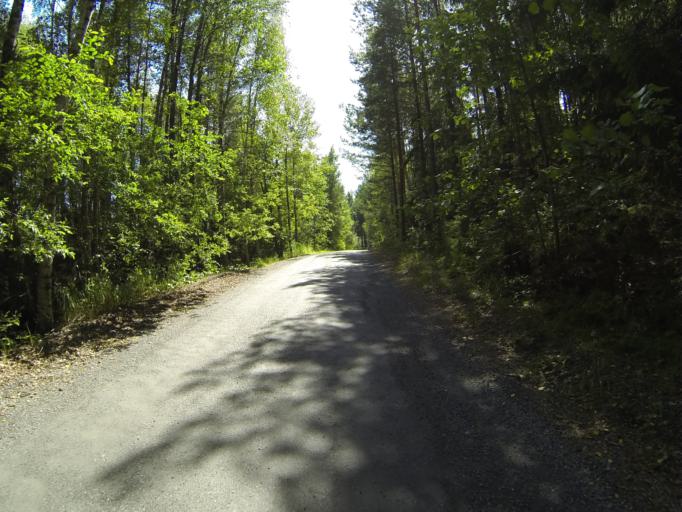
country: FI
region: Varsinais-Suomi
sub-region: Salo
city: Saerkisalo
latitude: 60.2632
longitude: 22.9734
